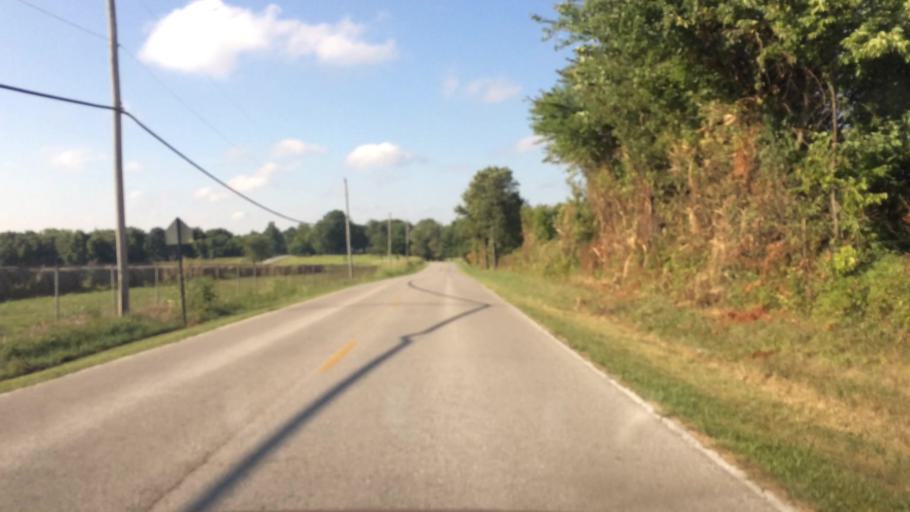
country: US
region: Missouri
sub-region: Greene County
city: Springfield
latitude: 37.2651
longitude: -93.2817
